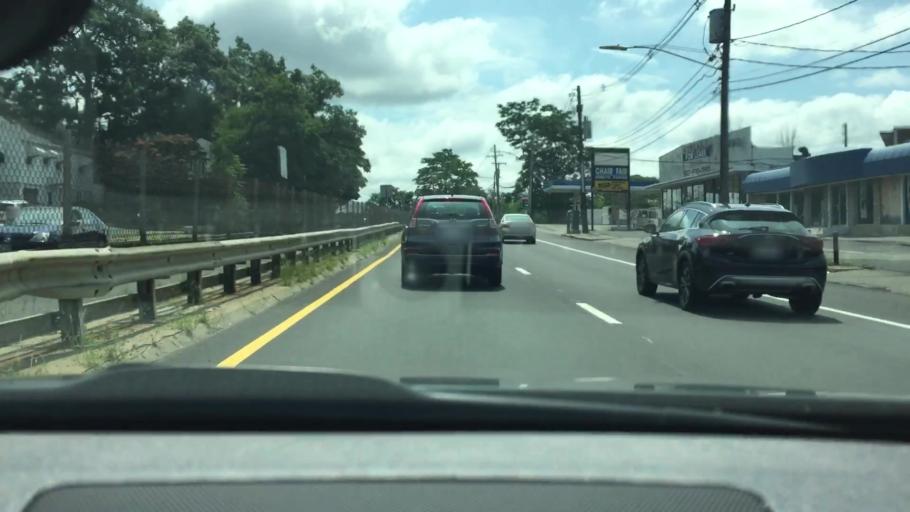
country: US
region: Massachusetts
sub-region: Norfolk County
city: Dedham
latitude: 42.2704
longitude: -71.1722
